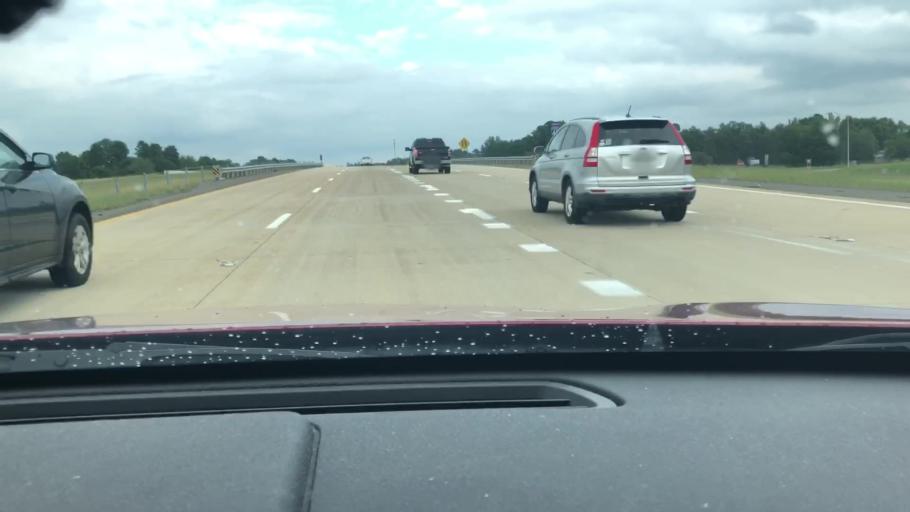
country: US
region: Texas
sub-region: Bowie County
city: Texarkana
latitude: 33.3926
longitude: -94.0146
